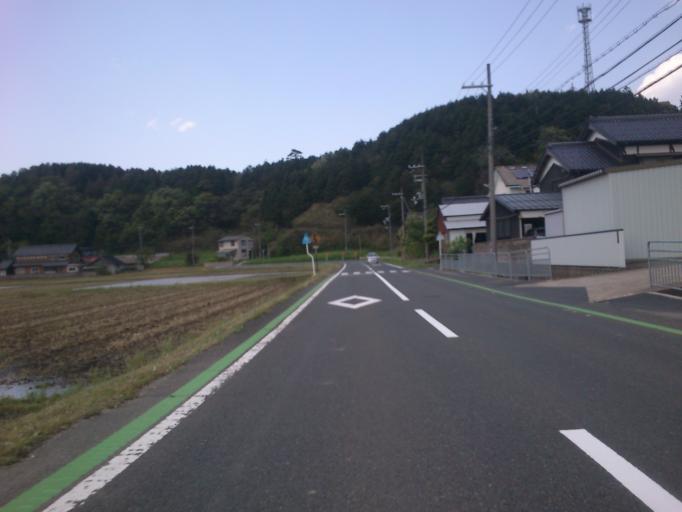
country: JP
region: Kyoto
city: Miyazu
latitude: 35.7245
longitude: 135.1069
